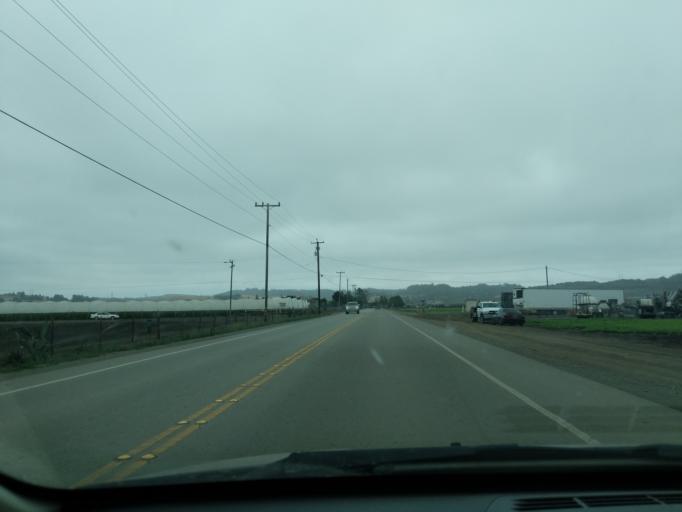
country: US
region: California
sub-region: San Benito County
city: Aromas
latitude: 36.9000
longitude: -121.6901
